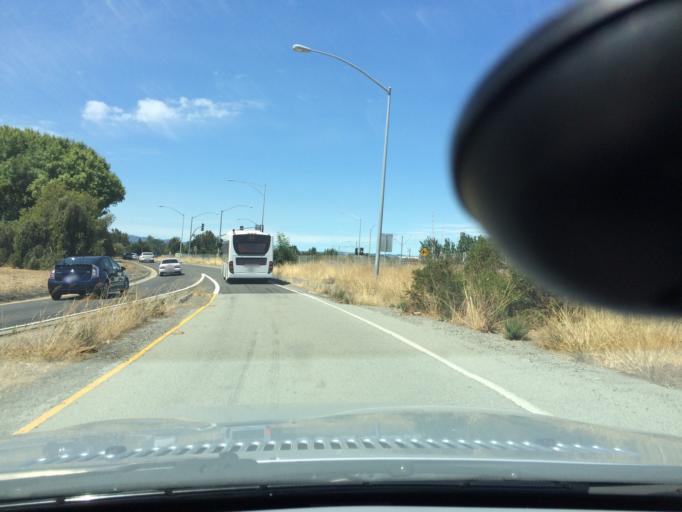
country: US
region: California
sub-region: Santa Clara County
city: Sunnyvale
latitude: 37.4021
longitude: -122.0352
